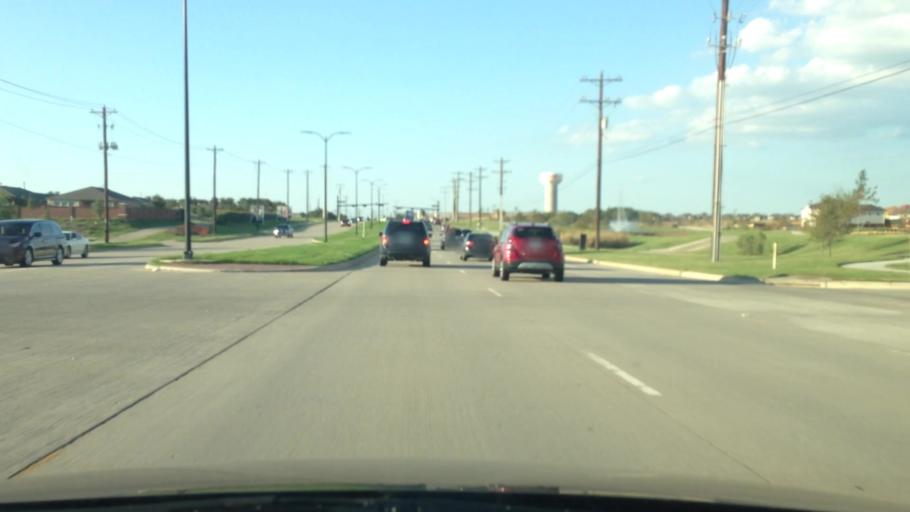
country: US
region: Texas
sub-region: Denton County
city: The Colony
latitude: 33.1329
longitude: -96.8907
